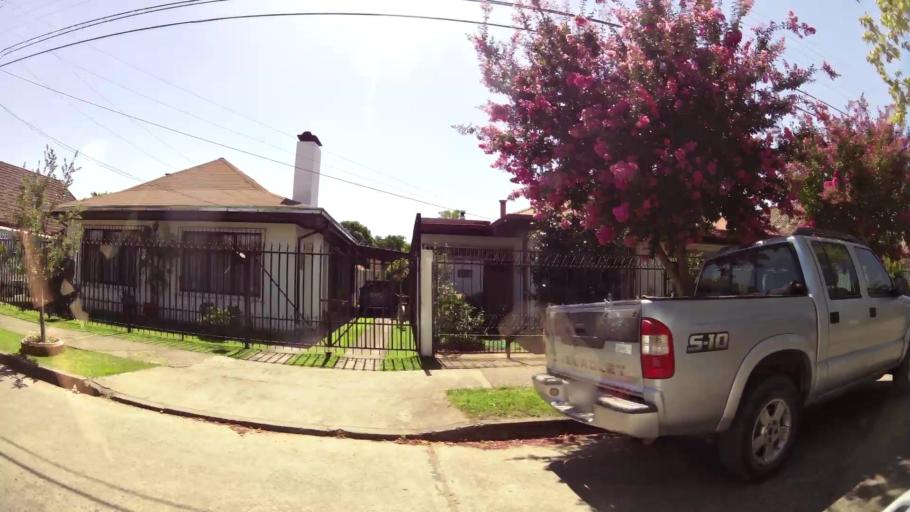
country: CL
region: Maule
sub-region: Provincia de Talca
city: Talca
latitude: -35.4141
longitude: -71.6549
